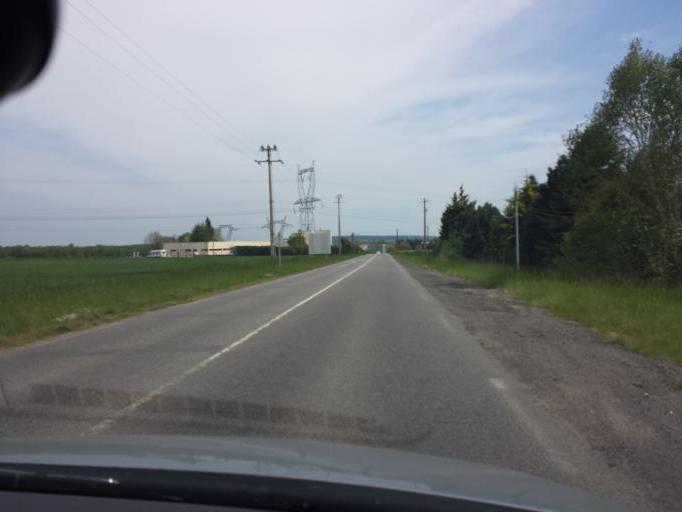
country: FR
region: Ile-de-France
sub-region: Departement des Yvelines
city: Thoiry
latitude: 48.8499
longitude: 1.8260
